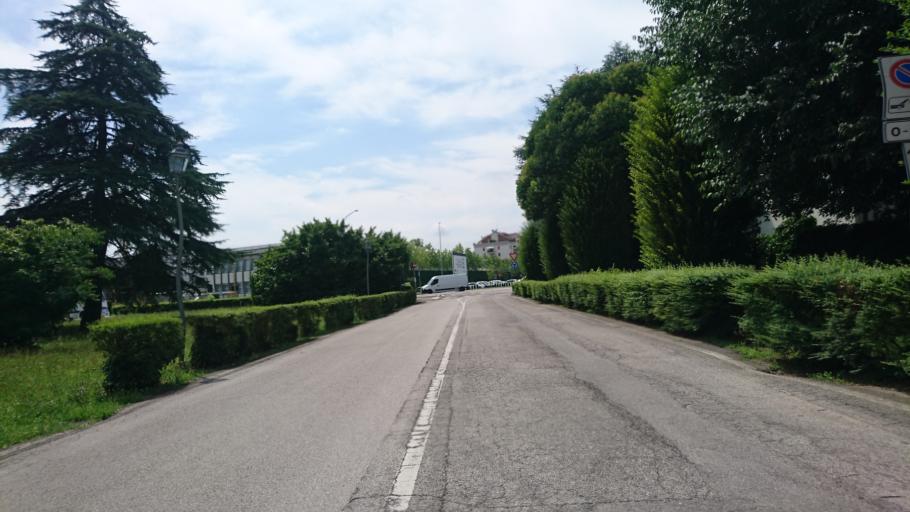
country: IT
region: Veneto
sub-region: Provincia di Padova
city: Caselle
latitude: 45.4115
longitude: 11.8486
